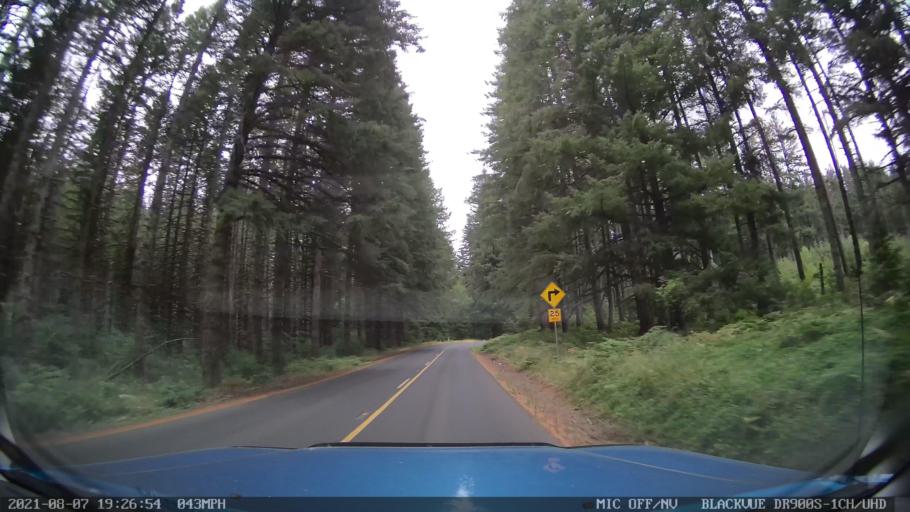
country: US
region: Oregon
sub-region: Linn County
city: Lyons
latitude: 44.8767
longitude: -122.6514
